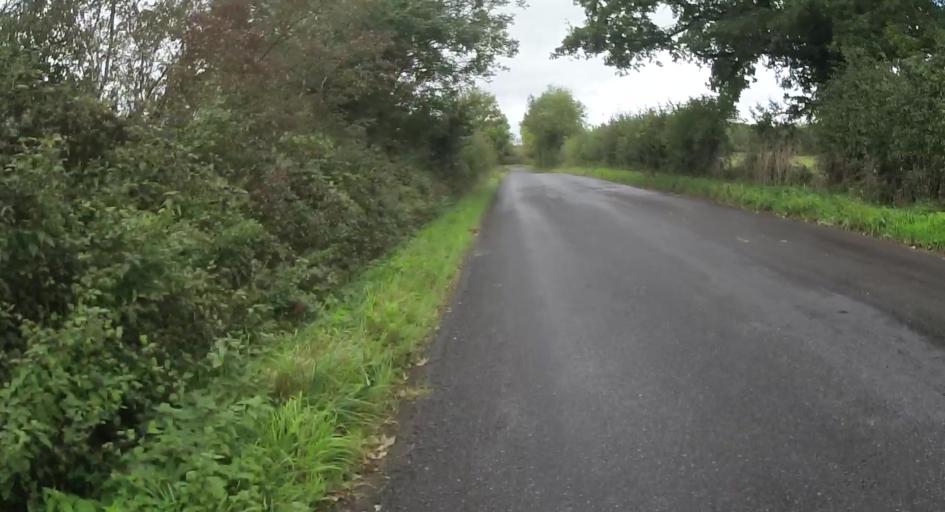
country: GB
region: England
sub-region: Hampshire
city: Tadley
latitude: 51.3876
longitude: -1.1776
